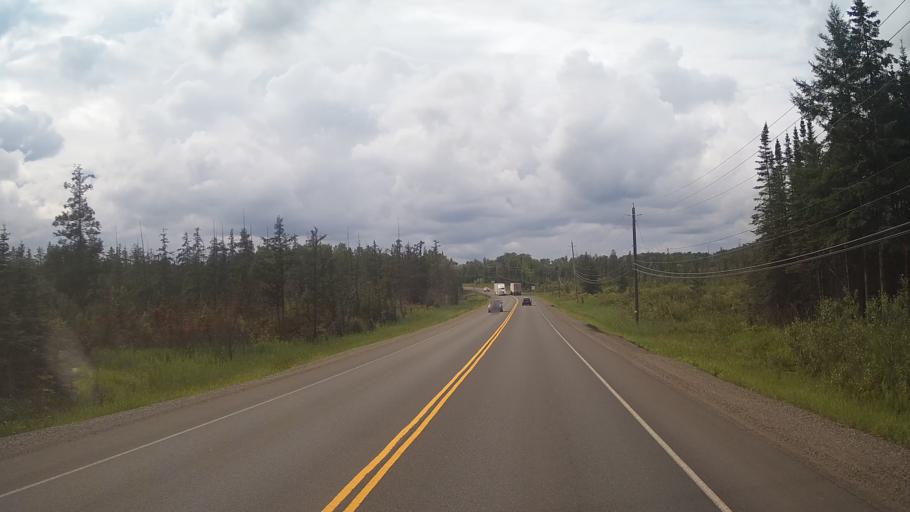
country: CA
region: Ontario
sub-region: Thunder Bay District
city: Thunder Bay
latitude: 48.4669
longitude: -89.2901
